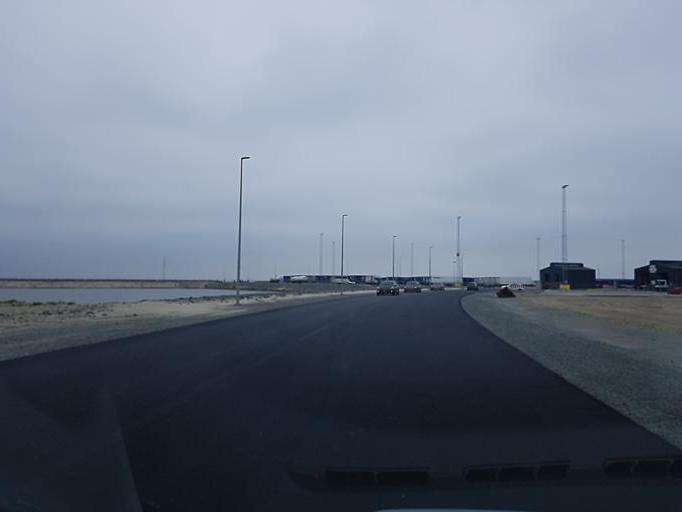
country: DK
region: South Denmark
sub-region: Esbjerg Kommune
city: Esbjerg
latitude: 55.4555
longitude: 8.4891
